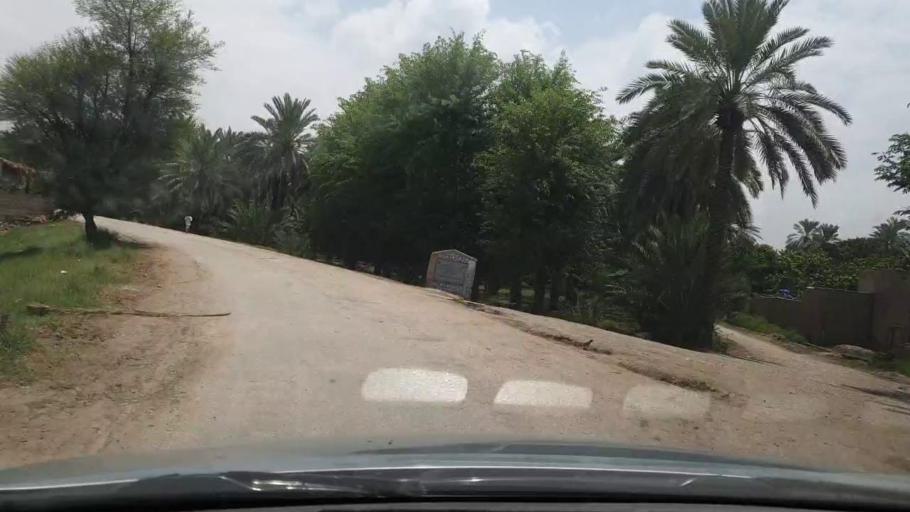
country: PK
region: Sindh
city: Khairpur
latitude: 27.4329
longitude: 68.7675
